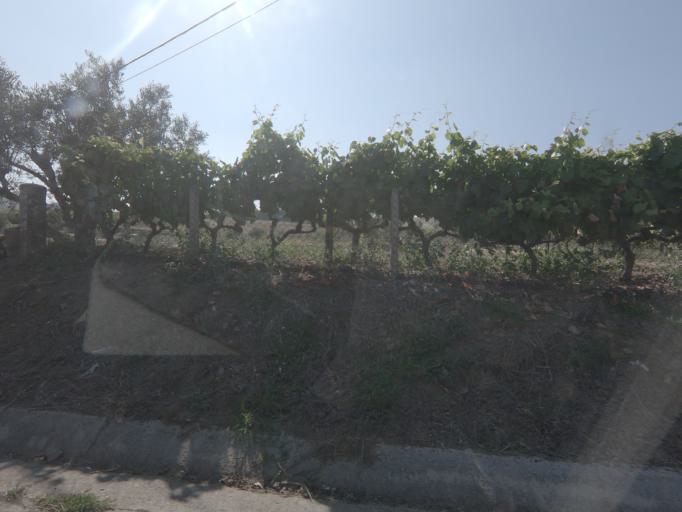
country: PT
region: Vila Real
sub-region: Sabrosa
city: Sabrosa
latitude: 41.2597
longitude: -7.5777
